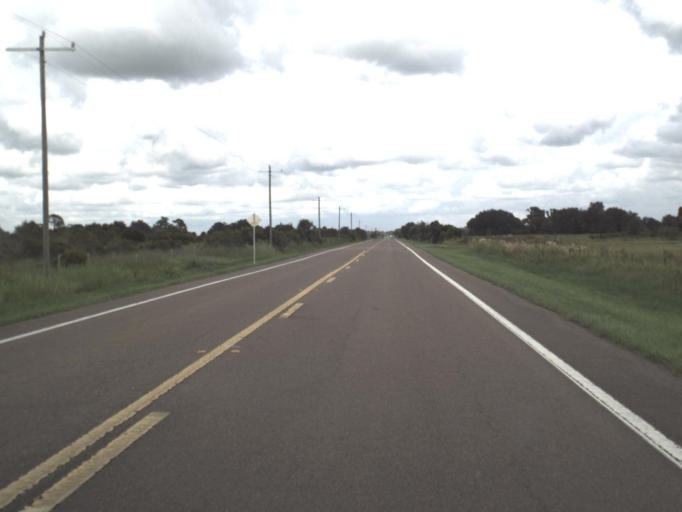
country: US
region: Florida
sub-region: DeSoto County
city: Nocatee
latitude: 27.1942
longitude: -82.0871
